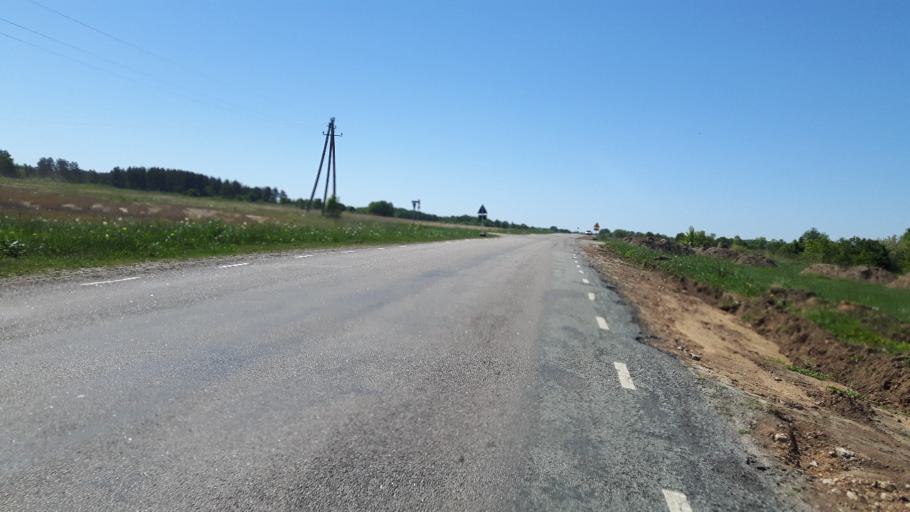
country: EE
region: Ida-Virumaa
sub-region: Narva-Joesuu linn
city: Narva-Joesuu
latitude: 59.4024
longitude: 27.9368
